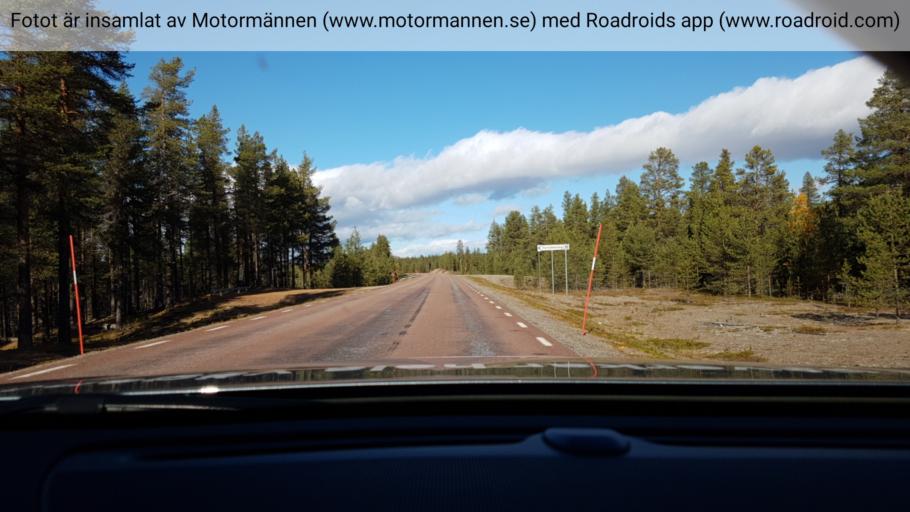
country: SE
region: Norrbotten
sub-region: Arjeplogs Kommun
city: Arjeplog
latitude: 66.0287
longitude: 18.0619
